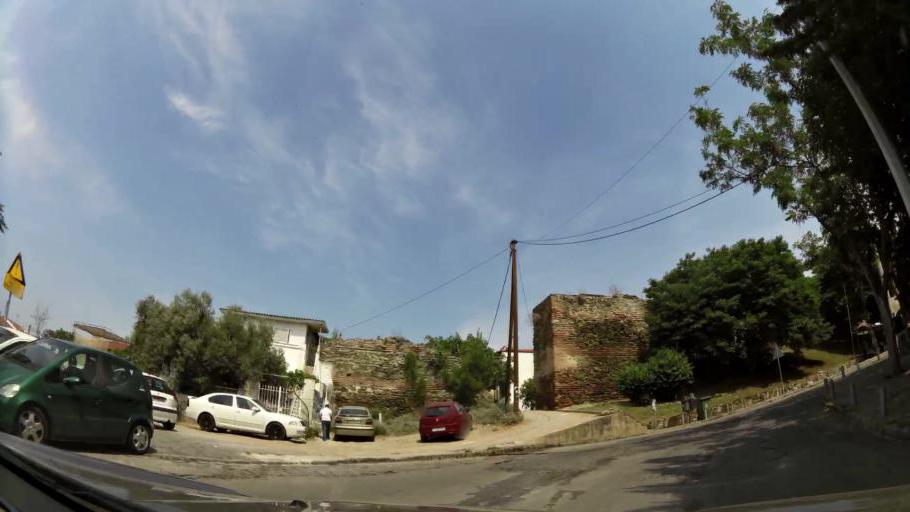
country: GR
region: Central Macedonia
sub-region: Nomos Thessalonikis
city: Agios Pavlos
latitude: 40.6367
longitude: 22.9577
